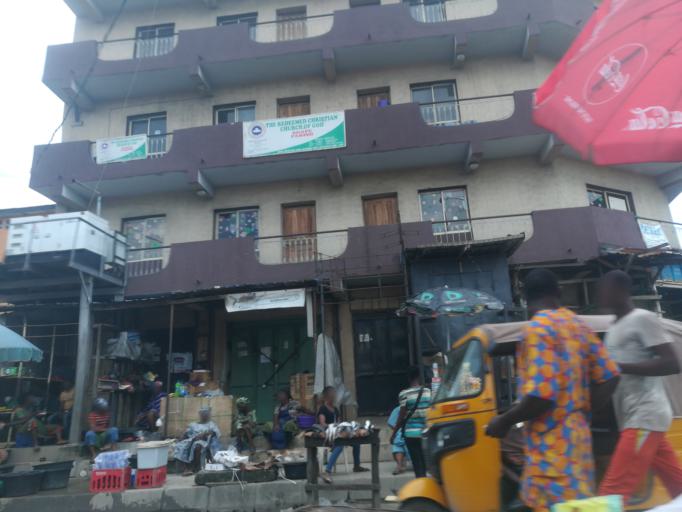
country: NG
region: Lagos
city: Lagos
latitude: 6.4588
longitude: 3.3923
